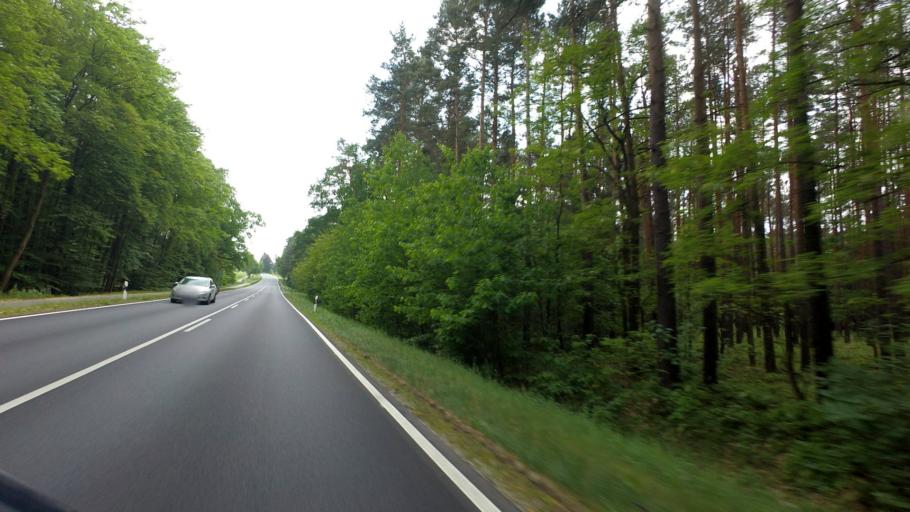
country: DE
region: Saxony
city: Rietschen
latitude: 51.3691
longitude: 14.7955
